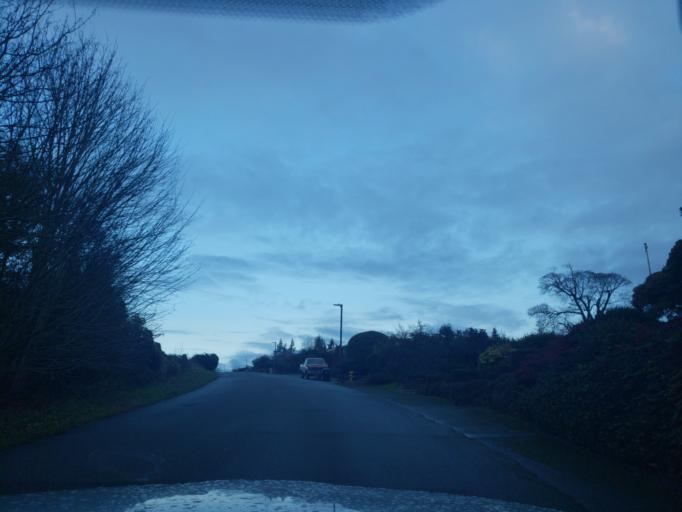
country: US
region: Washington
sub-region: Snohomish County
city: Woodway
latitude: 47.7616
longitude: -122.3800
